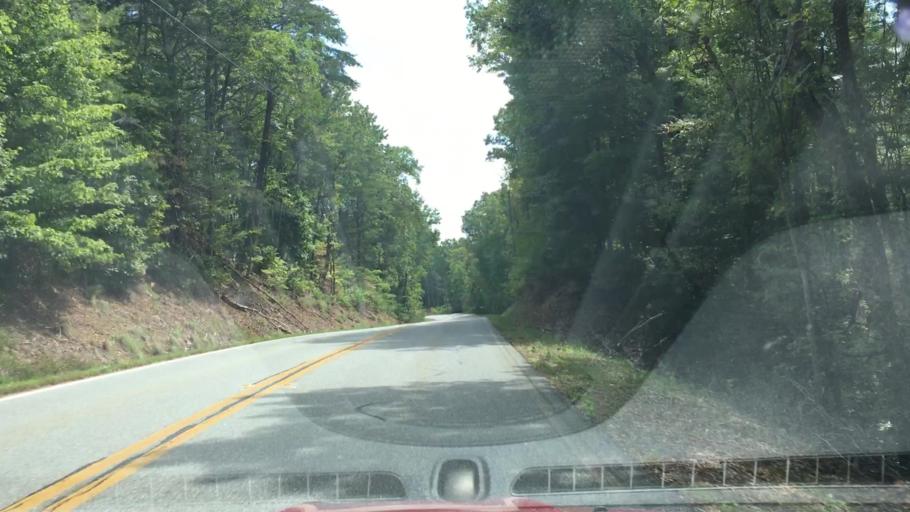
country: US
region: Georgia
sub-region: Murray County
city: Chatsworth
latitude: 34.7856
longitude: -84.6229
